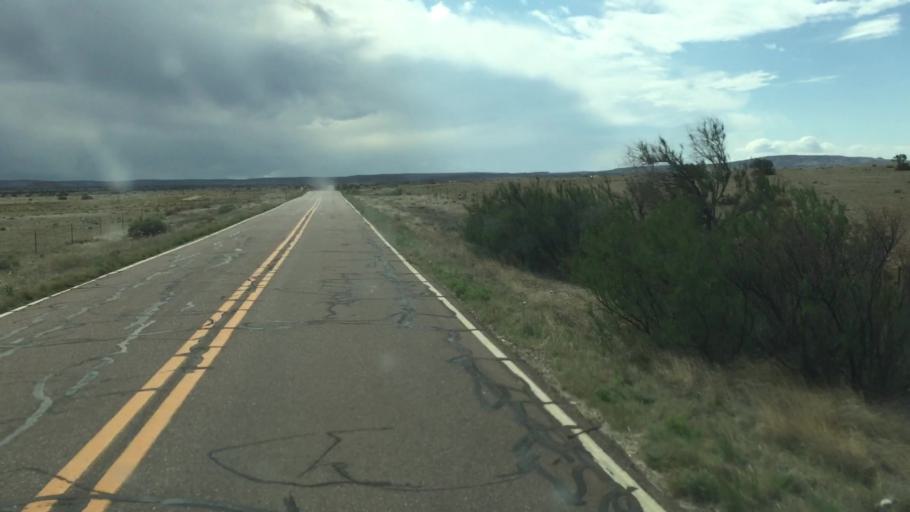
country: US
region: Arizona
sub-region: Navajo County
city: White Mountain Lake
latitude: 34.5169
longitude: -109.7061
